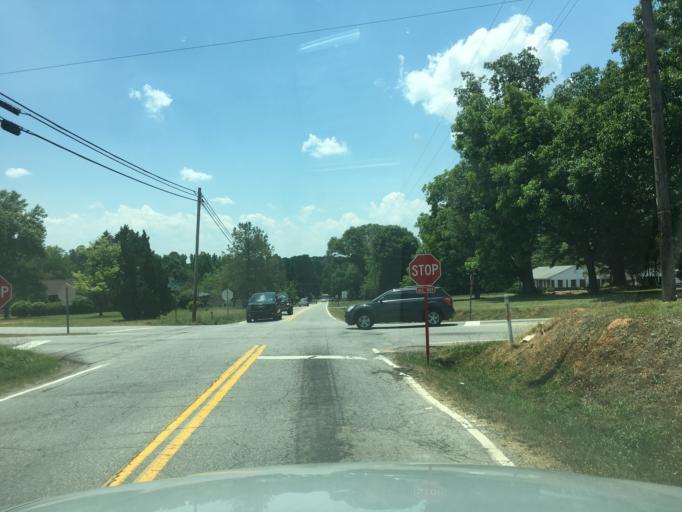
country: US
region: South Carolina
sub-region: Anderson County
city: Anderson
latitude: 34.5223
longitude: -82.6278
